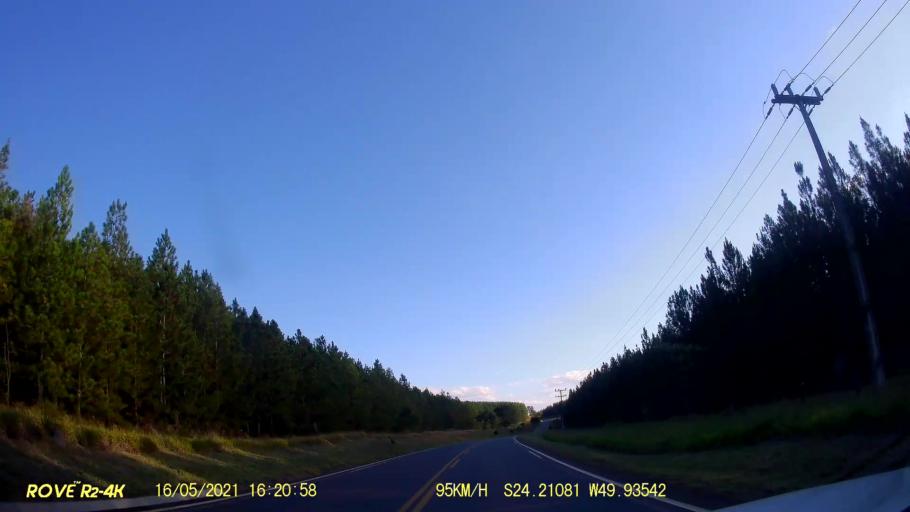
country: BR
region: Parana
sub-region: Jaguariaiva
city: Jaguariaiva
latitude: -24.2110
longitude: -49.9355
